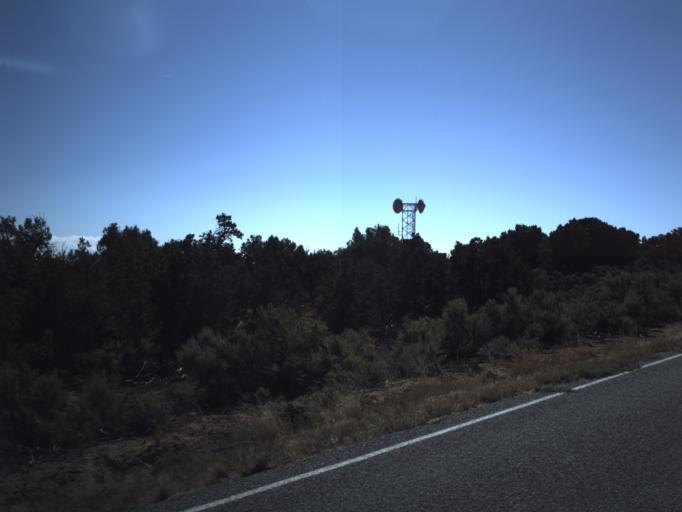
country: US
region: Utah
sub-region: San Juan County
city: Blanding
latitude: 37.2958
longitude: -109.9340
